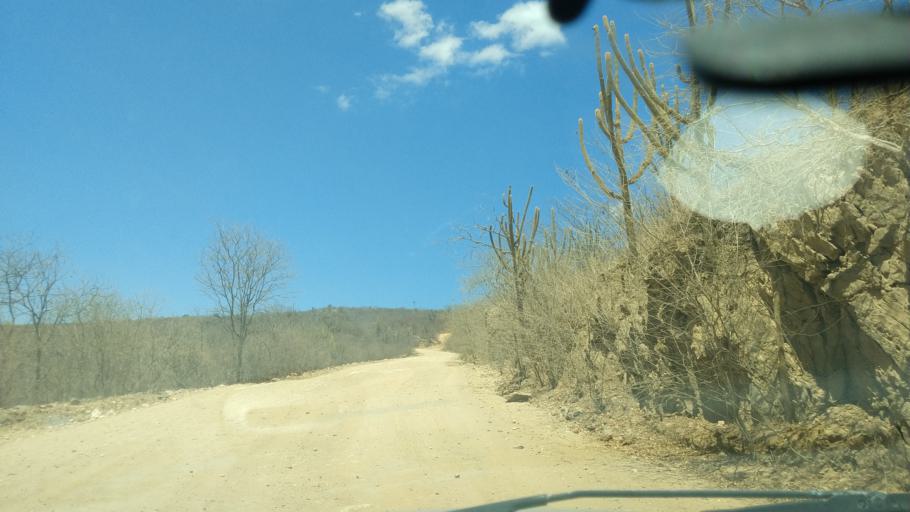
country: BR
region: Rio Grande do Norte
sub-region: Cerro Cora
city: Cerro Cora
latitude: -6.0159
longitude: -36.3142
